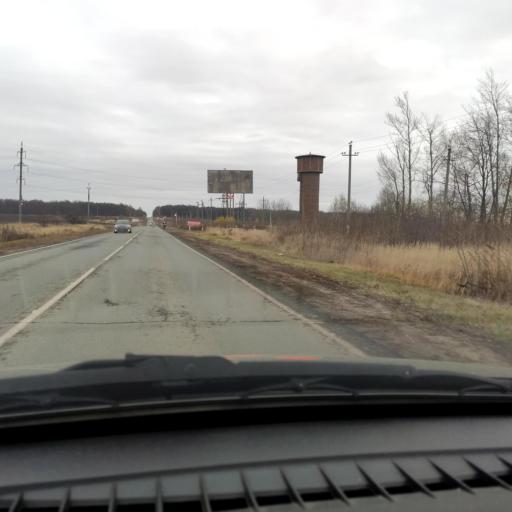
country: RU
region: Samara
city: Zhigulevsk
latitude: 53.3403
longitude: 49.4728
